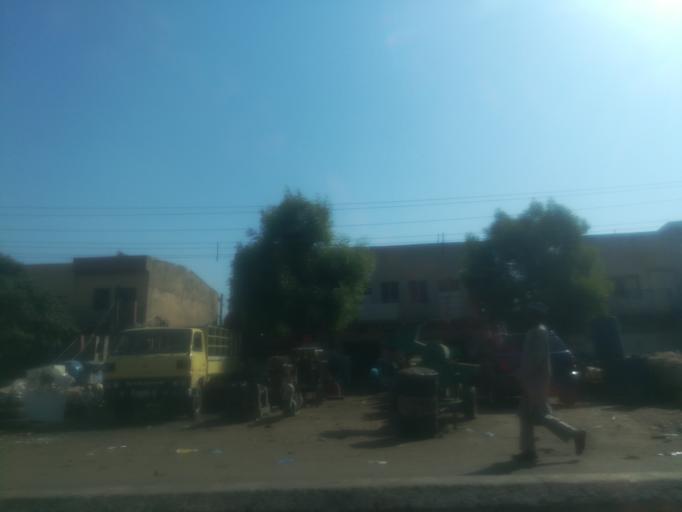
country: NG
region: Kano
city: Kano
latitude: 12.0132
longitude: 8.5326
